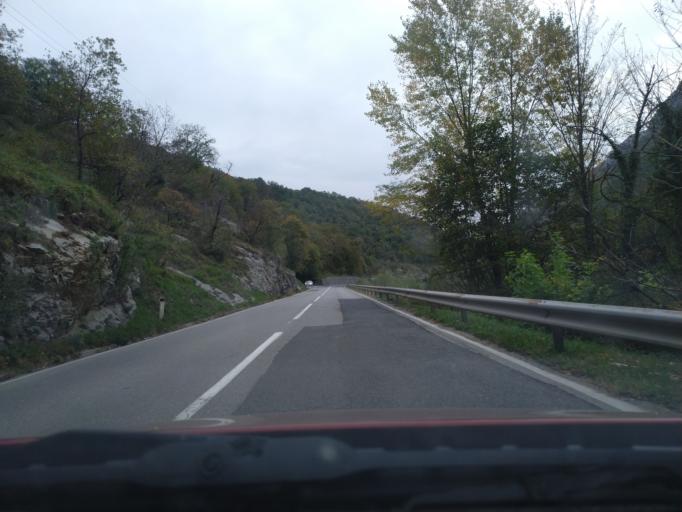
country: SI
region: Nova Gorica
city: Solkan
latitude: 46.0056
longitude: 13.6274
